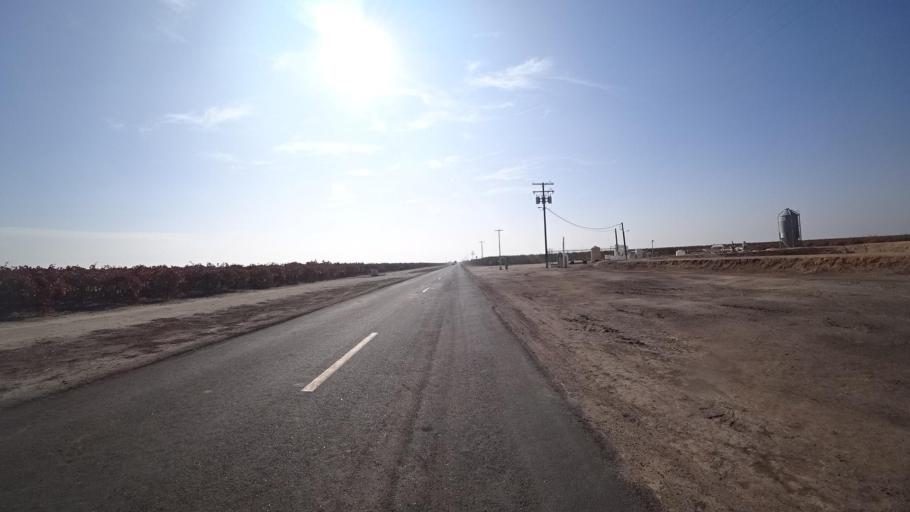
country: US
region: California
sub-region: Kern County
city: McFarland
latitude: 35.6866
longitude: -119.1692
